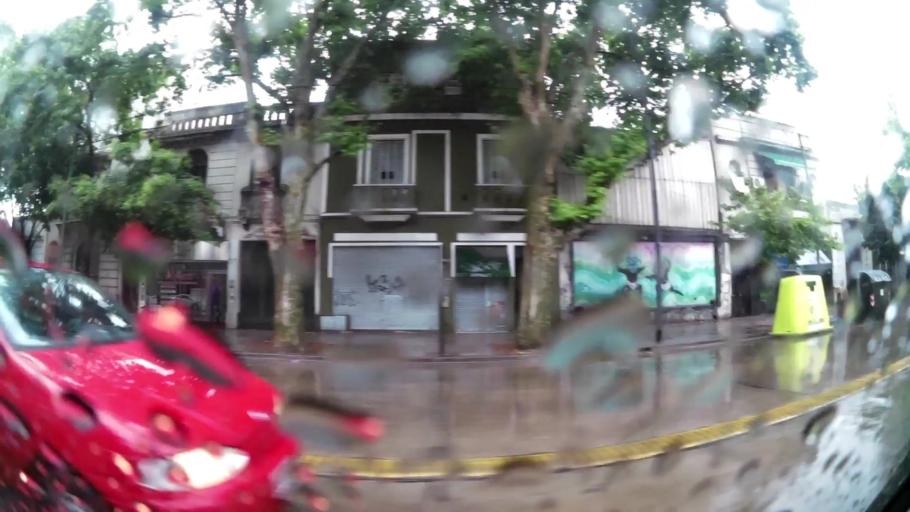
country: AR
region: Buenos Aires
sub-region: Partido de Avellaneda
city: Avellaneda
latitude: -34.6437
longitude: -58.3687
